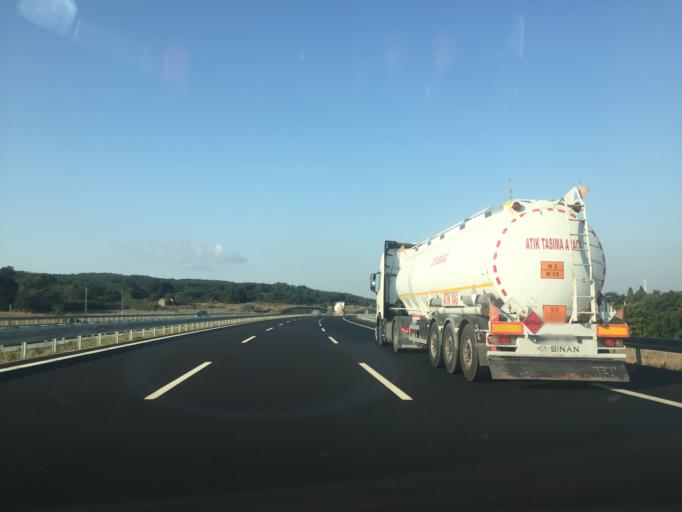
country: TR
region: Balikesir
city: Savastepe
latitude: 39.4837
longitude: 27.6527
